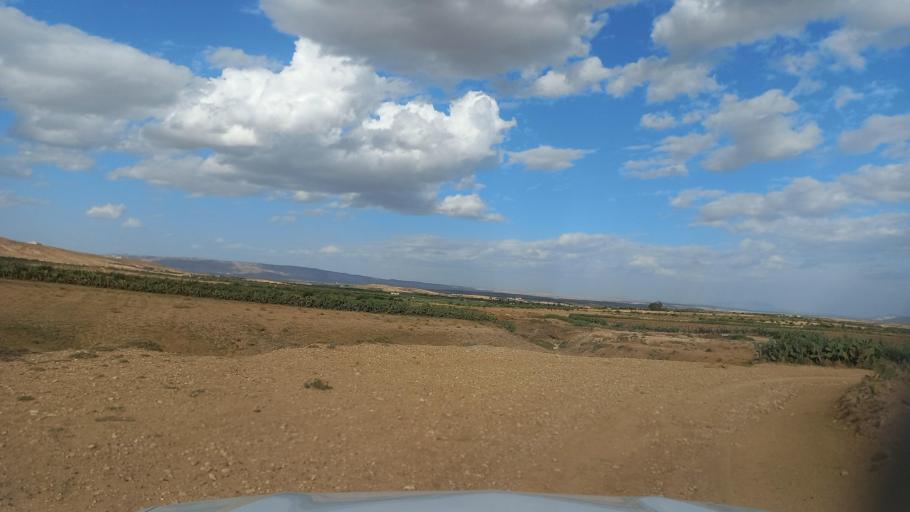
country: TN
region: Al Qasrayn
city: Sbiba
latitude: 35.4537
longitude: 9.0916
